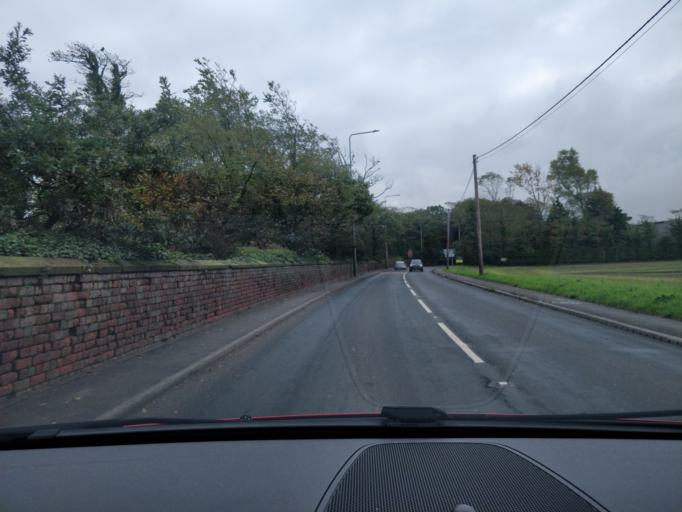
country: GB
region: England
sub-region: Lancashire
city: Ormskirk
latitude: 53.6080
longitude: -2.9334
